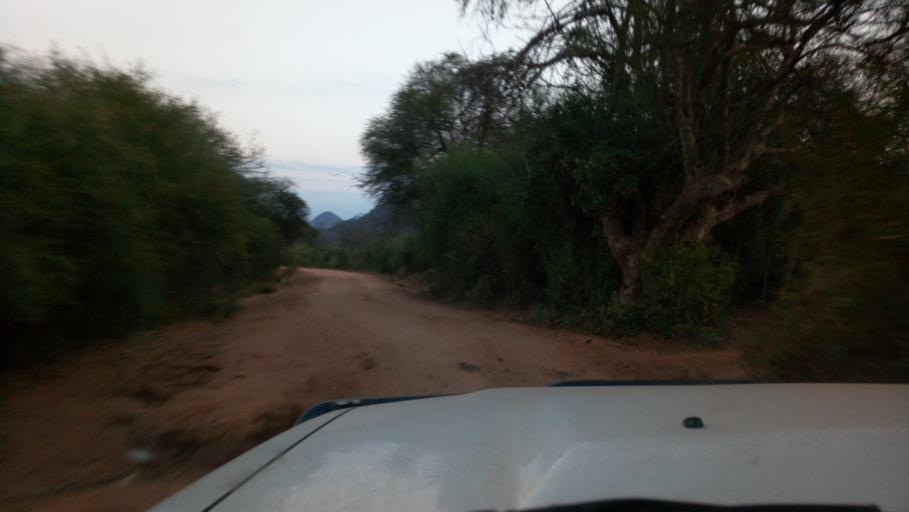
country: KE
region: Kitui
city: Kitui
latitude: -1.7380
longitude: 38.2022
